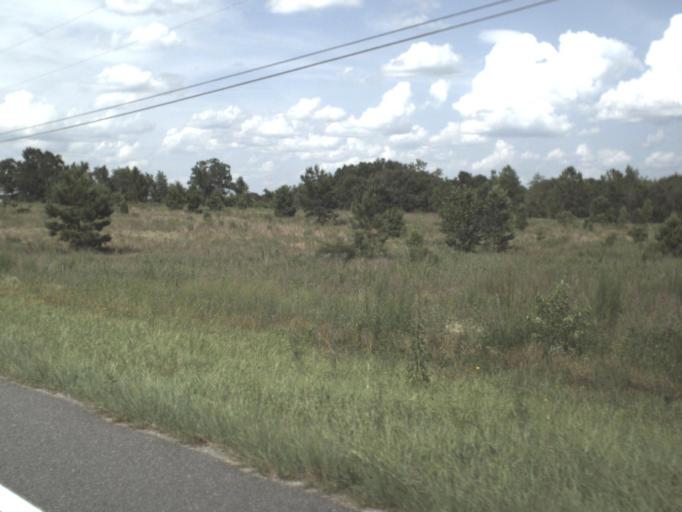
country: US
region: Florida
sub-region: Columbia County
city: Lake City
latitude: 30.0371
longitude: -82.7078
